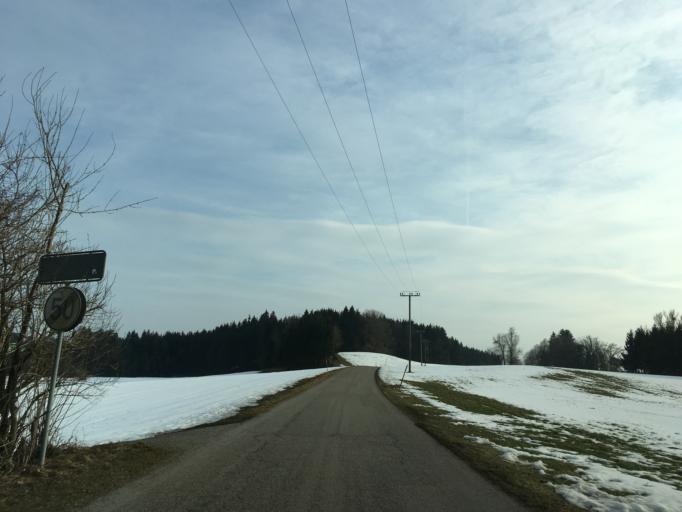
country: DE
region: Bavaria
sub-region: Upper Bavaria
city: Halfing
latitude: 47.9408
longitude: 12.2599
